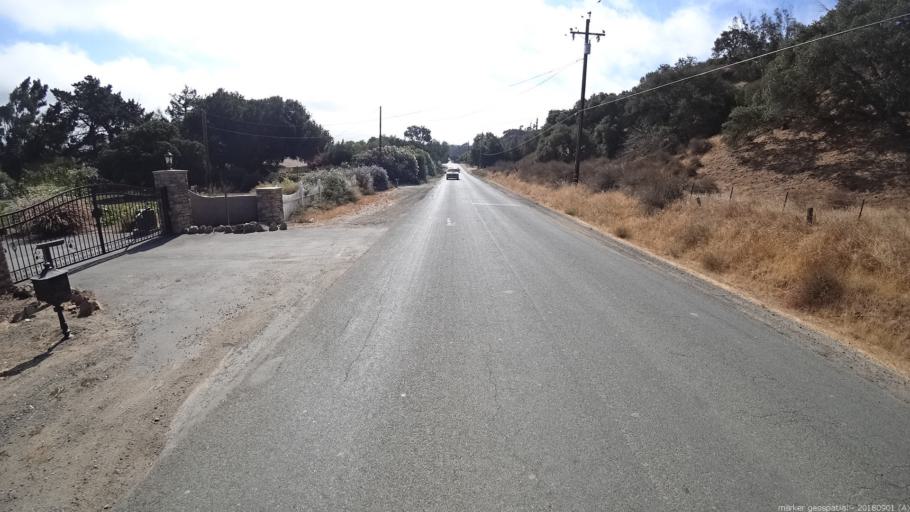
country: US
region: California
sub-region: Monterey County
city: Soledad
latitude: 36.3887
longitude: -121.3637
